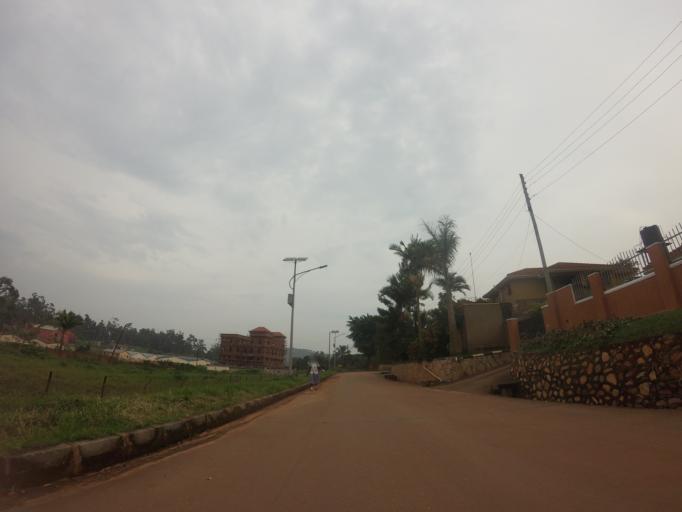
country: UG
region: Central Region
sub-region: Wakiso District
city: Kireka
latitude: 0.3482
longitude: 32.6222
